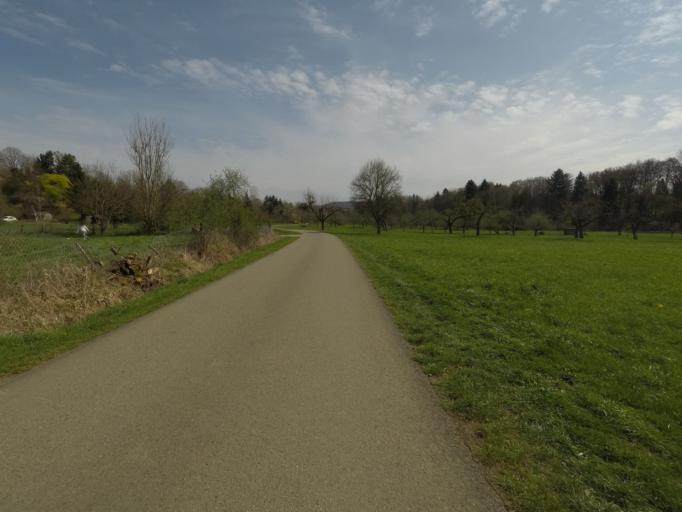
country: DE
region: Baden-Wuerttemberg
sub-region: Tuebingen Region
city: Reutlingen
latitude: 48.4854
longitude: 9.1728
